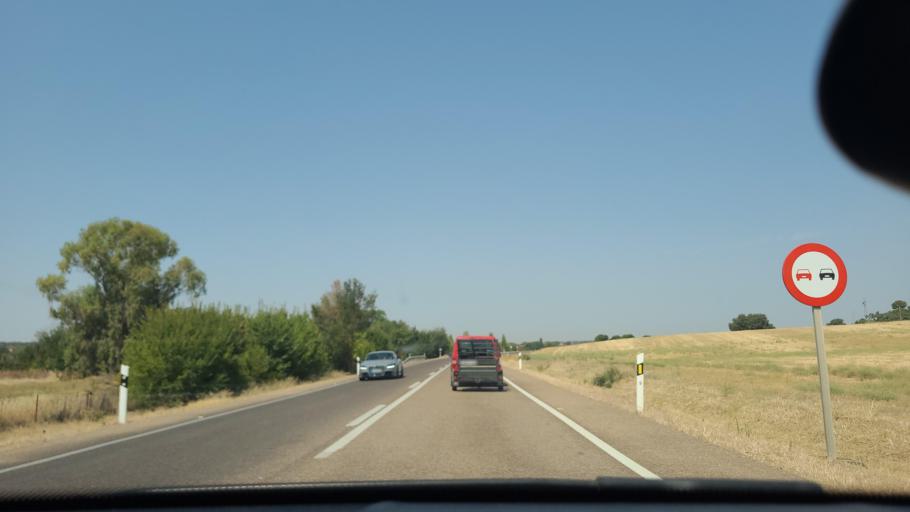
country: ES
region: Extremadura
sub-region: Provincia de Badajoz
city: Badajoz
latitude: 38.8128
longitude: -6.8958
